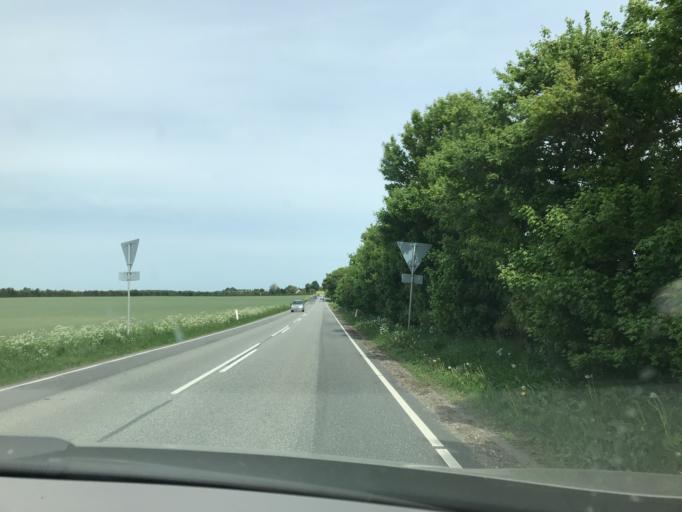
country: DK
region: Central Jutland
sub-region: Norddjurs Kommune
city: Allingabro
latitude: 56.4478
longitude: 10.2867
